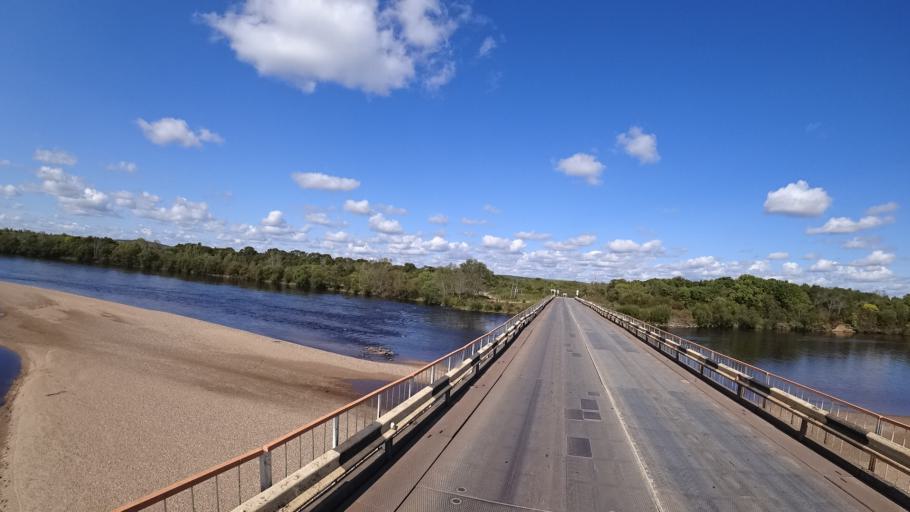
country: RU
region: Amur
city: Arkhara
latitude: 49.3975
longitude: 130.1351
